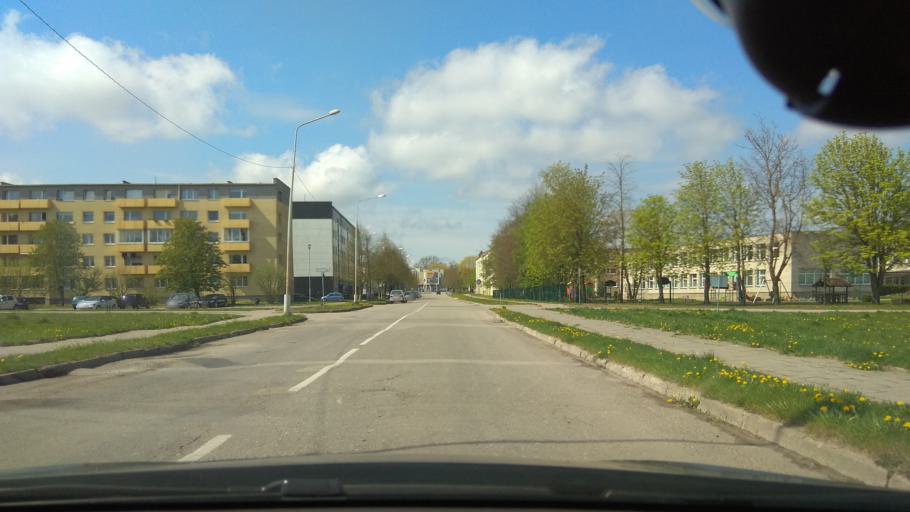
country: LT
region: Siauliu apskritis
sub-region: Joniskis
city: Joniskis
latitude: 56.2421
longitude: 23.6228
